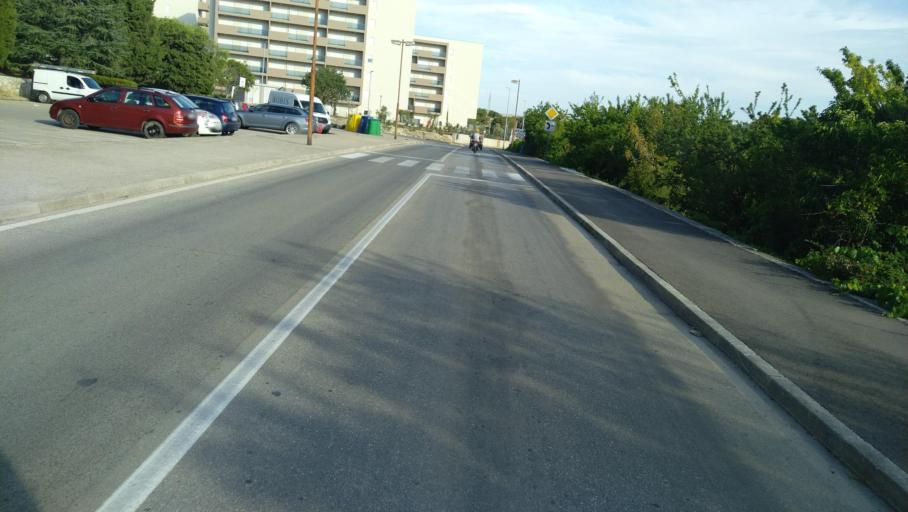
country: HR
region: Sibensko-Kniniska
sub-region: Grad Sibenik
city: Sibenik
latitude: 43.7203
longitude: 15.9112
